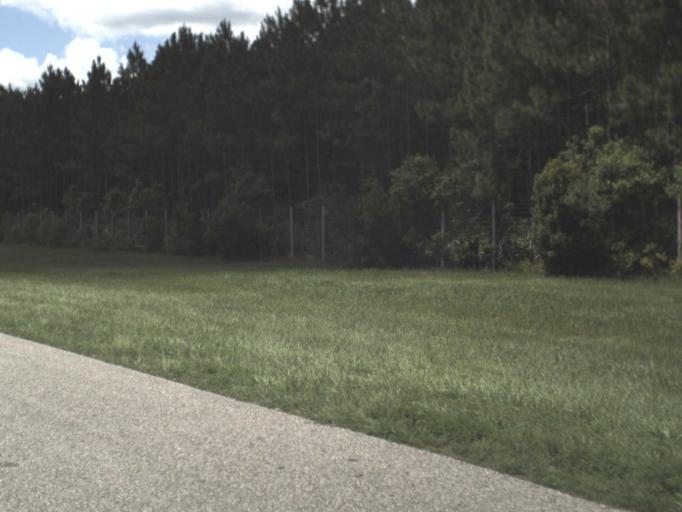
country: US
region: Florida
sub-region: Saint Johns County
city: Saint Augustine Shores
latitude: 29.7640
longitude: -81.3532
